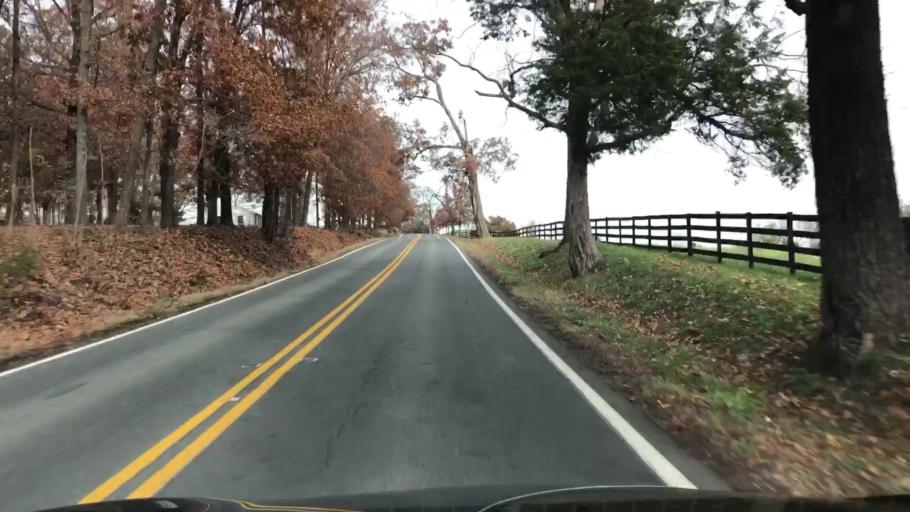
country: US
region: Virginia
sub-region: Fauquier County
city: New Baltimore
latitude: 38.7645
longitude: -77.6807
